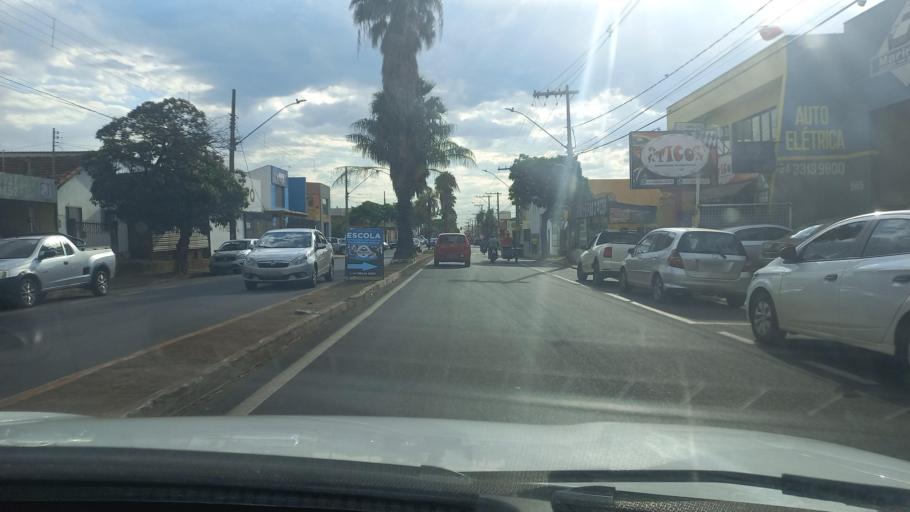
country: BR
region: Minas Gerais
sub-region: Uberaba
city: Uberaba
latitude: -19.7686
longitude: -47.9256
